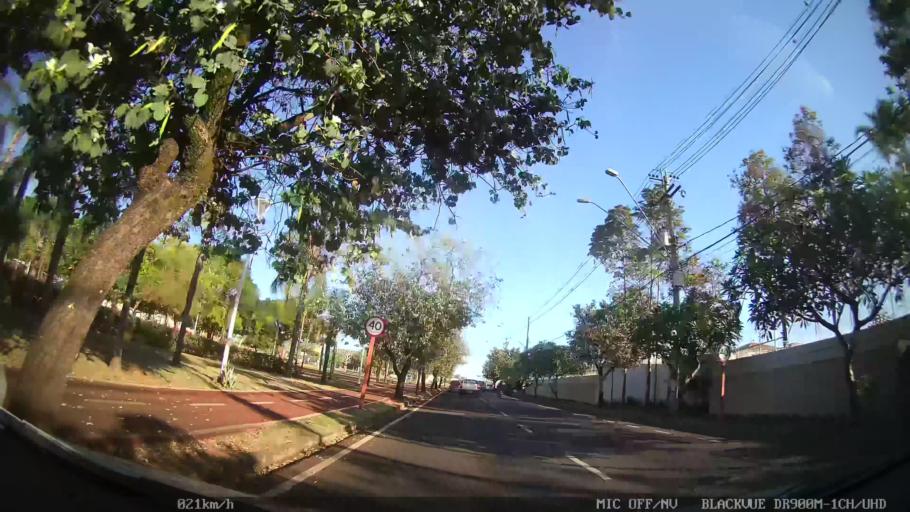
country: BR
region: Sao Paulo
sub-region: Sao Jose Do Rio Preto
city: Sao Jose do Rio Preto
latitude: -20.8496
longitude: -49.4132
